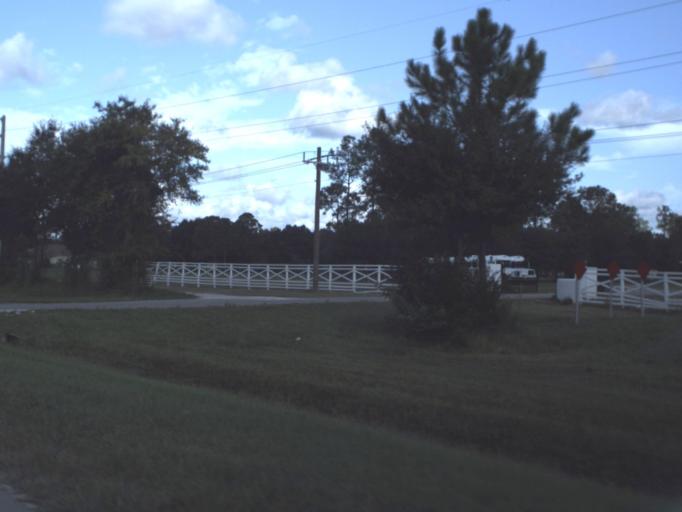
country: US
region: Florida
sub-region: DeSoto County
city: Southeast Arcadia
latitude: 27.2088
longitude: -81.7923
